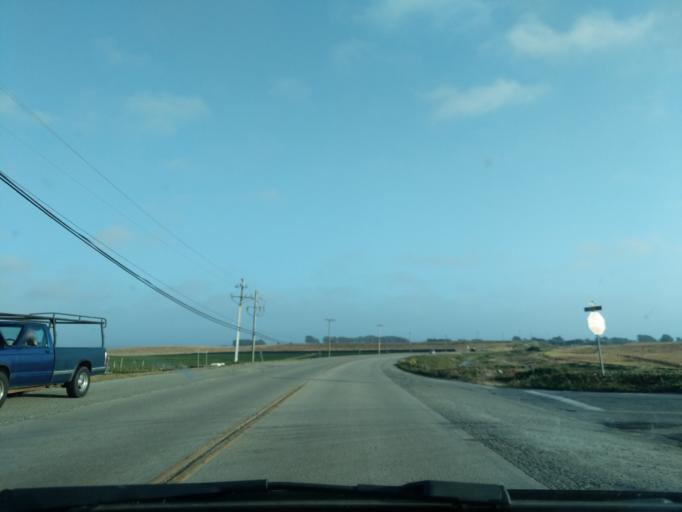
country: US
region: California
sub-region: Monterey County
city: Marina
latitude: 36.7053
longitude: -121.7886
